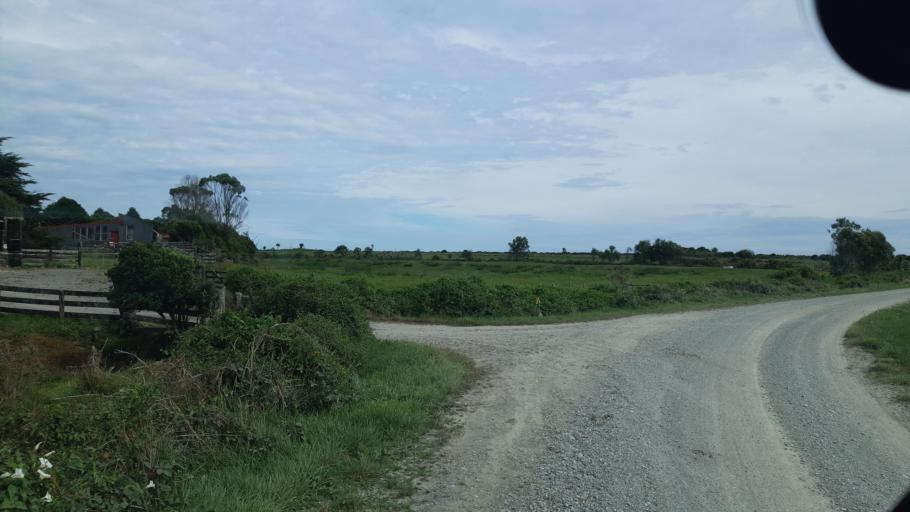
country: NZ
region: West Coast
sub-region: Westland District
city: Hokitika
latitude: -42.9086
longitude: 170.7574
